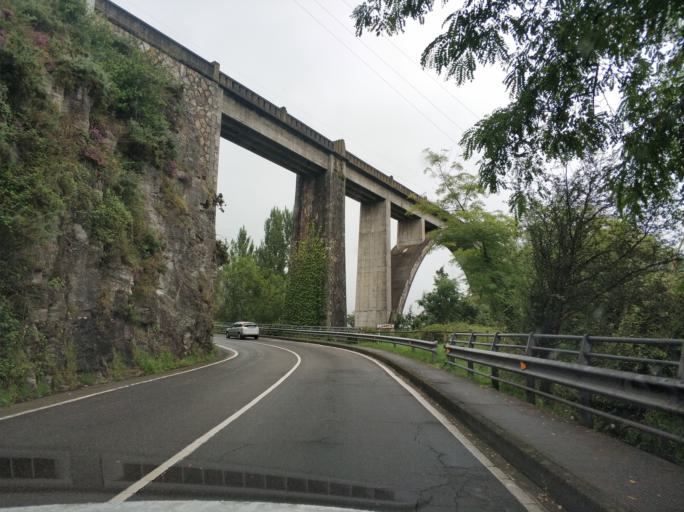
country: ES
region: Asturias
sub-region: Province of Asturias
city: Navia
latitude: 43.5402
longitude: -6.5351
